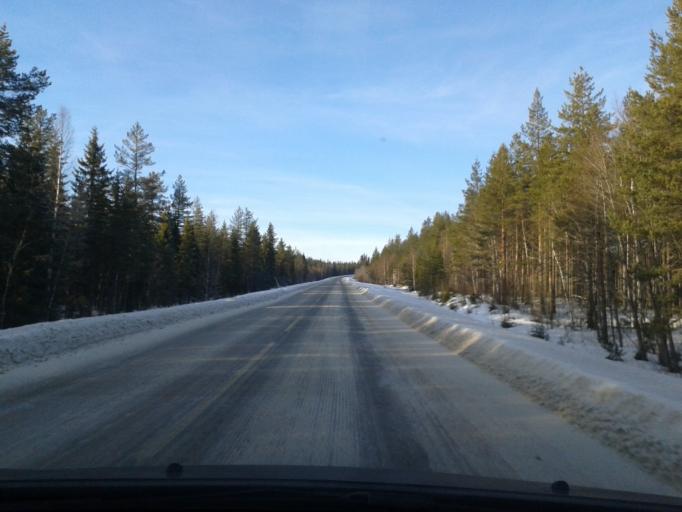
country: SE
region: Vaesternorrland
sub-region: OErnskoeldsviks Kommun
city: Bredbyn
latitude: 63.7601
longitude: 17.6942
